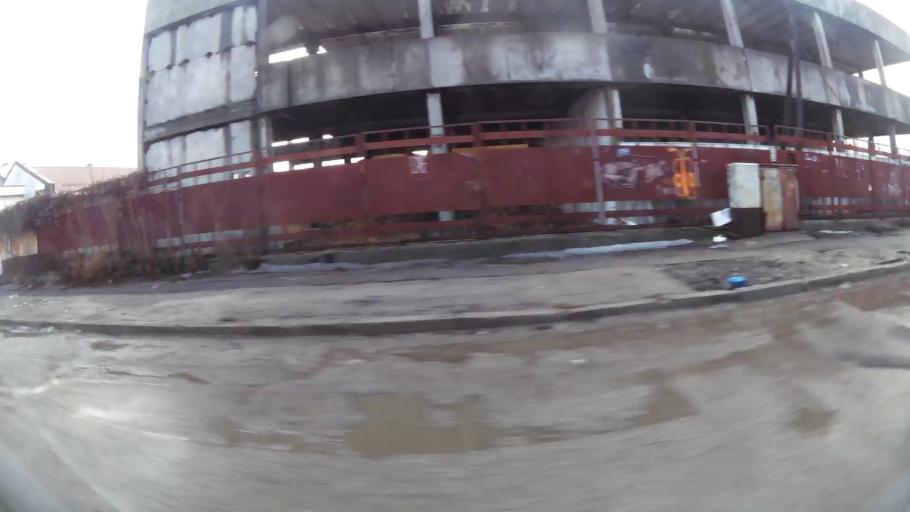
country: BG
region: Sofia-Capital
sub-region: Stolichna Obshtina
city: Sofia
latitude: 42.7258
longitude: 23.3173
